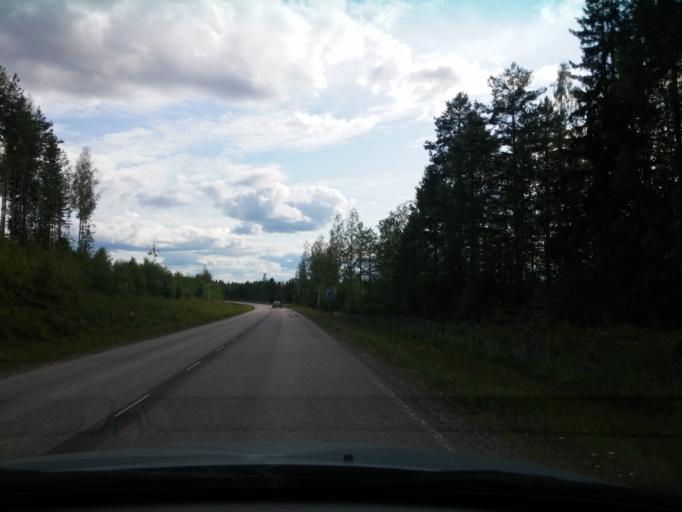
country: FI
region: Central Finland
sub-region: Keuruu
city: Multia
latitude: 62.3648
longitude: 24.7402
